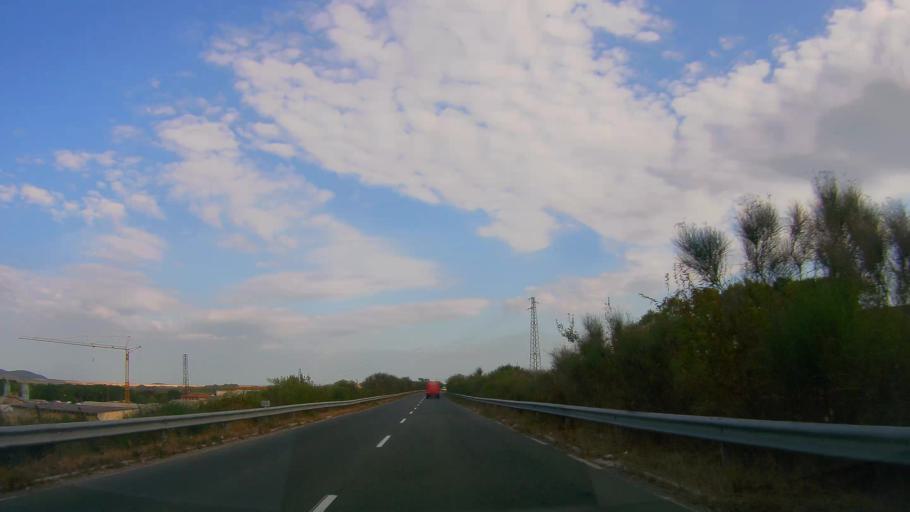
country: BG
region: Burgas
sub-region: Obshtina Sozopol
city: Sozopol
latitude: 42.3936
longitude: 27.6760
